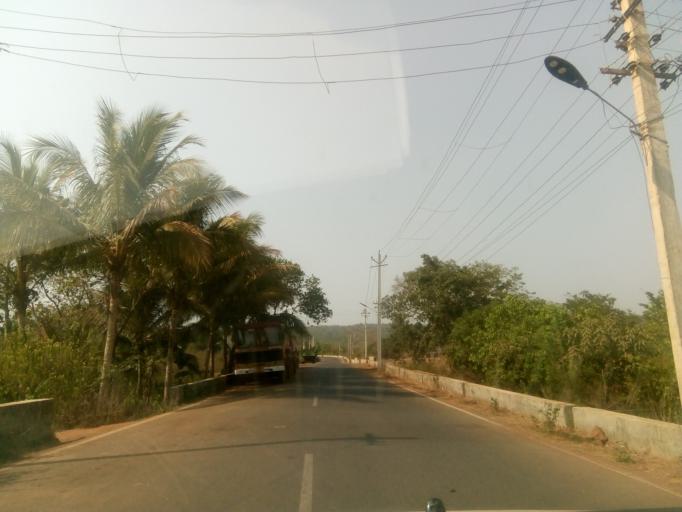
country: IN
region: Goa
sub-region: North Goa
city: Pernem
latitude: 15.7094
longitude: 73.8541
